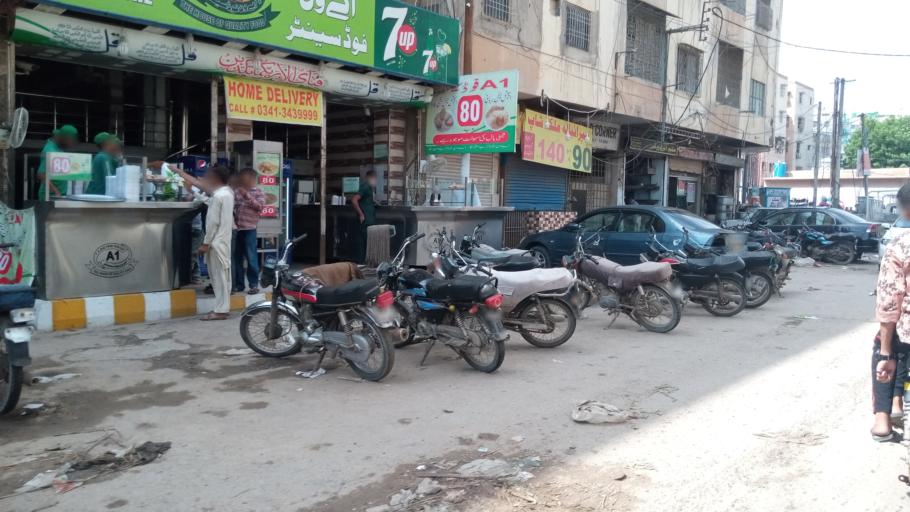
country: PK
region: Sindh
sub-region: Karachi District
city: Karachi
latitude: 24.9268
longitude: 67.0677
